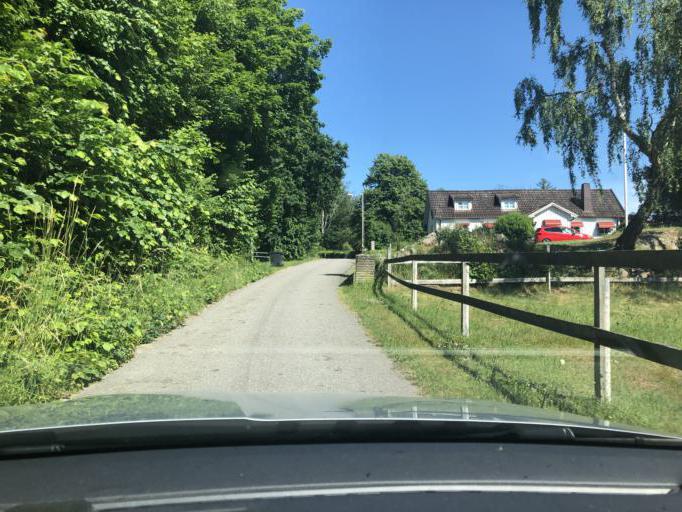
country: SE
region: Blekinge
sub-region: Karlshamns Kommun
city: Morrum
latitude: 56.1903
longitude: 14.6833
